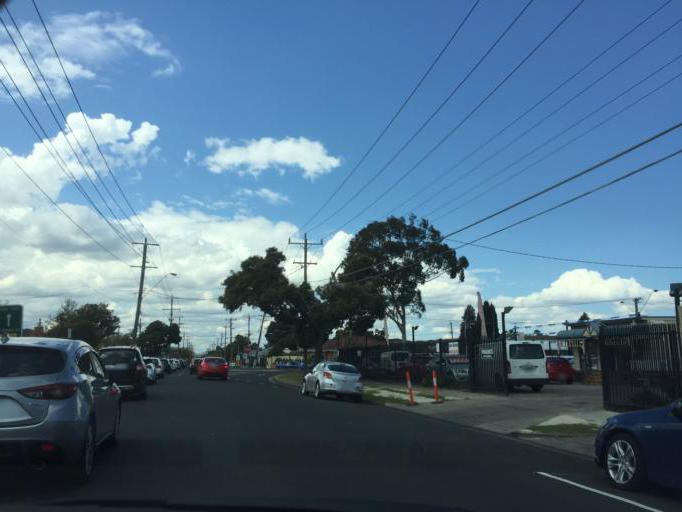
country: AU
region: Victoria
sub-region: Maribyrnong
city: Maidstone
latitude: -37.7816
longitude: 144.8688
